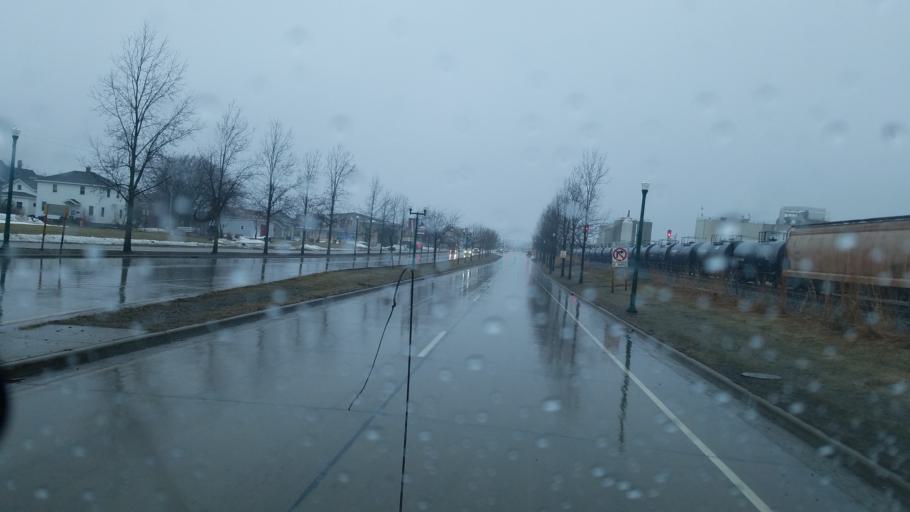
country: US
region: Wisconsin
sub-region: Wood County
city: Marshfield
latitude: 44.6654
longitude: -90.1684
